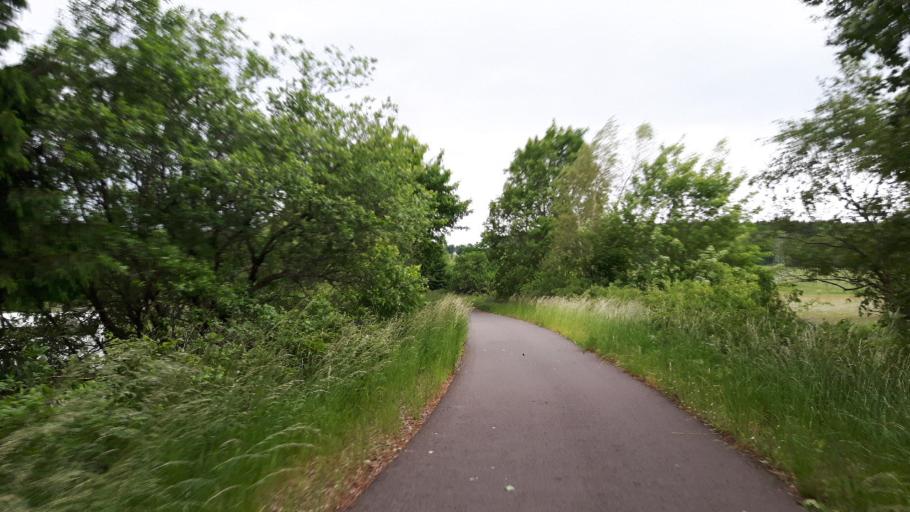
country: DE
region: Thuringia
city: Grossbreitenbach
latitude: 50.5868
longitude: 10.9924
